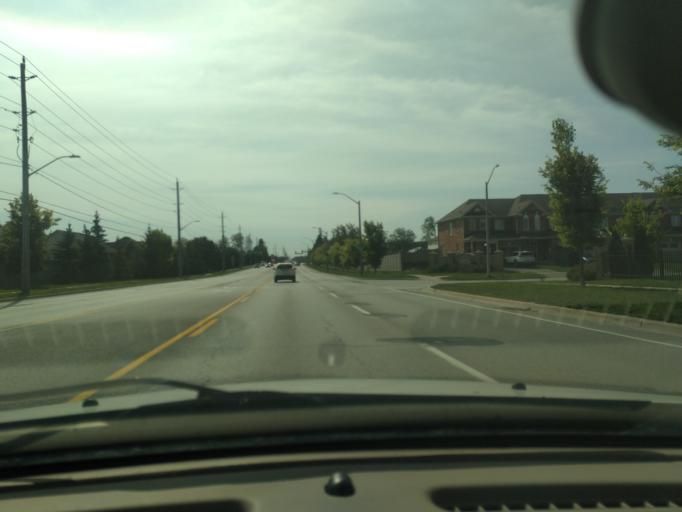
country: CA
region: Ontario
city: Innisfil
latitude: 44.3421
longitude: -79.7012
